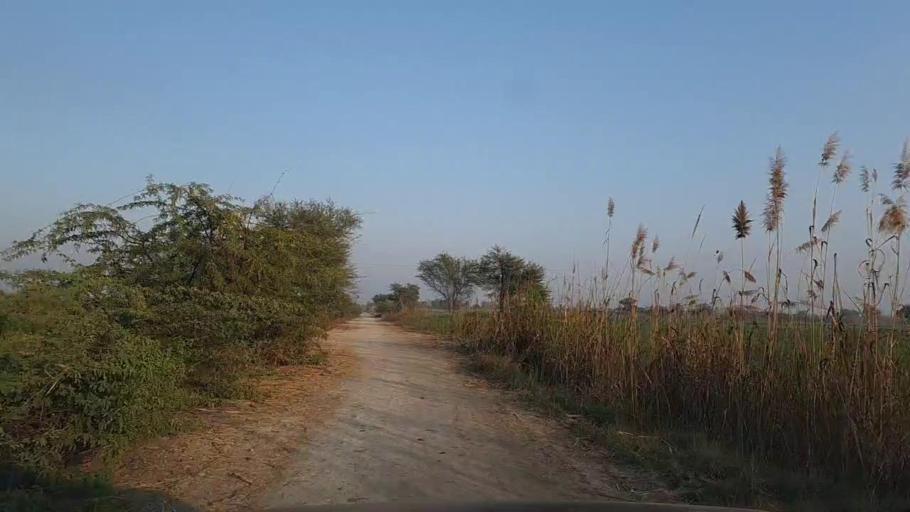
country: PK
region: Sindh
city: Daur
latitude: 26.4874
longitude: 68.4203
